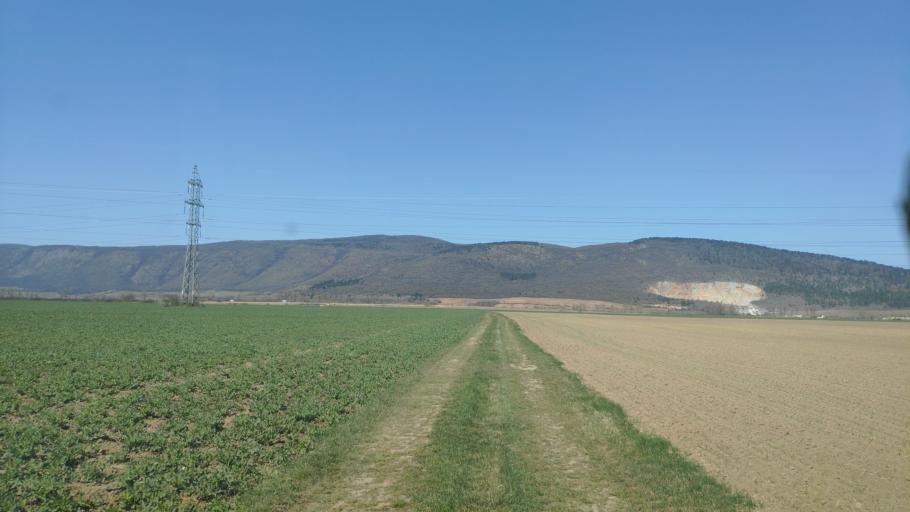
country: SK
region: Kosicky
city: Moldava nad Bodvou
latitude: 48.5979
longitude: 20.9324
